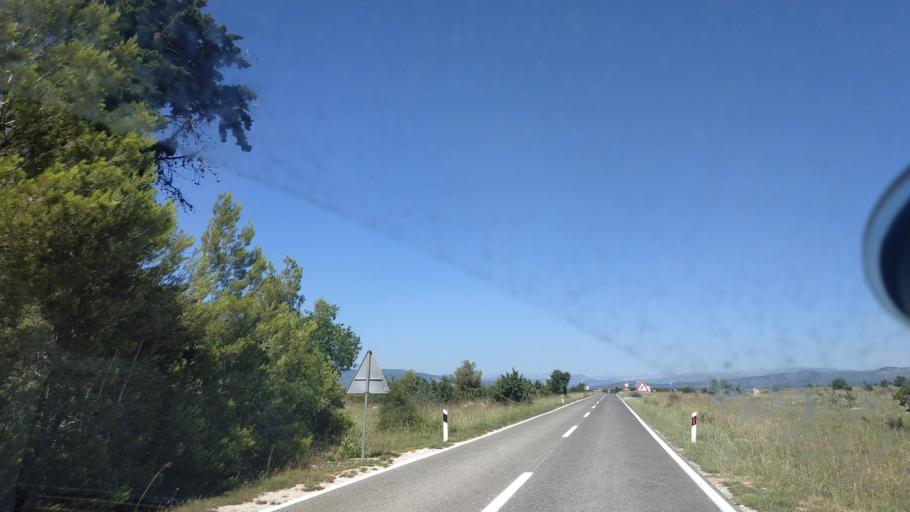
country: HR
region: Sibensko-Kniniska
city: Drnis
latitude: 43.8182
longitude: 16.0592
